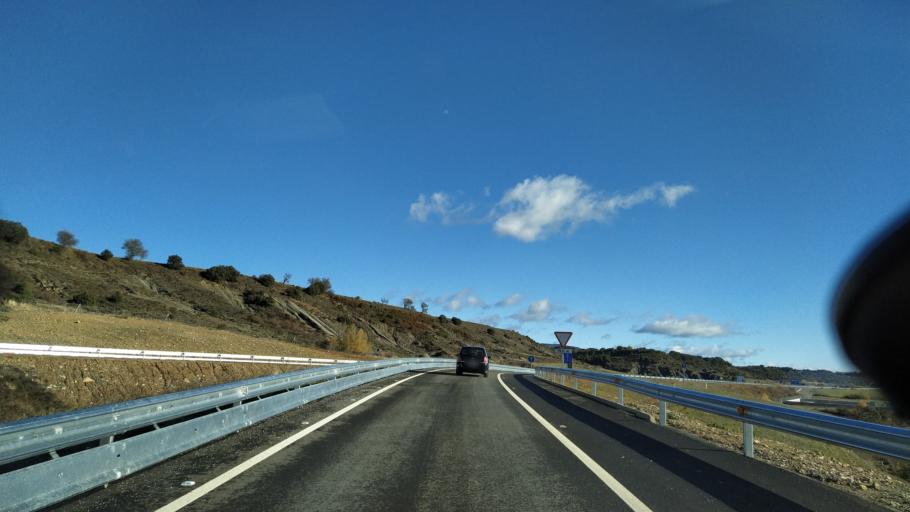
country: ES
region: Aragon
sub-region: Provincia de Huesca
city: Santa Cruz de la Seros
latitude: 42.5643
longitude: -0.7094
